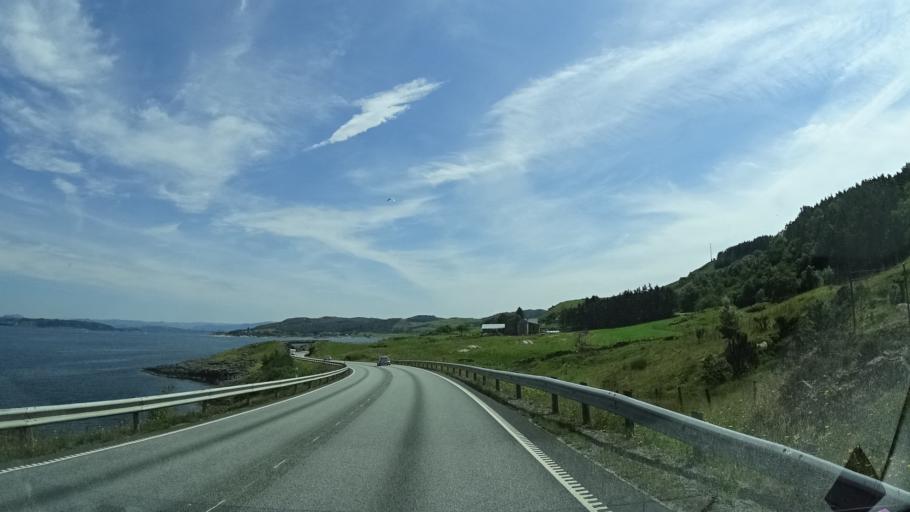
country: NO
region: Rogaland
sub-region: Rennesoy
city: Vikevag
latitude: 59.1254
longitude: 5.6644
